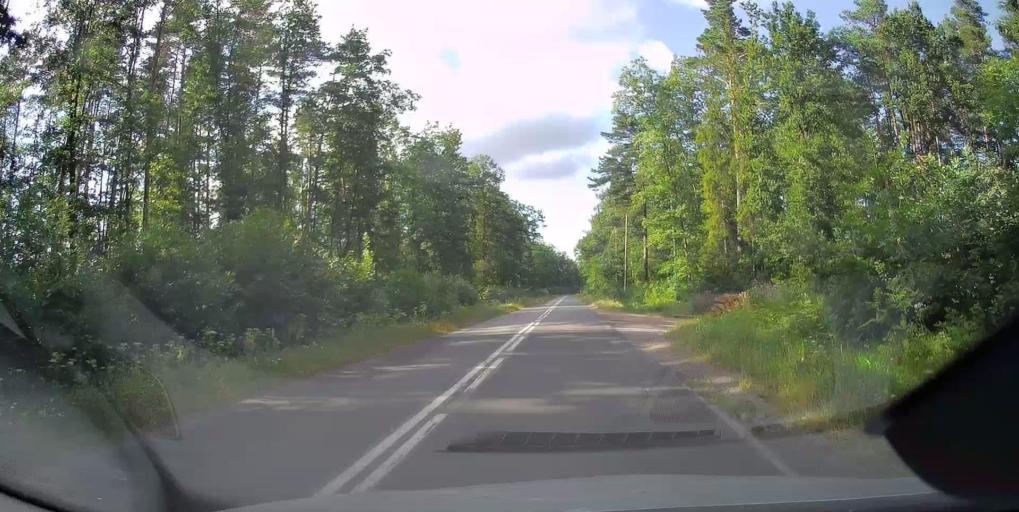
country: PL
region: Swietokrzyskie
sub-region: Powiat skarzyski
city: Suchedniow
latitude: 51.0180
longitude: 20.8391
